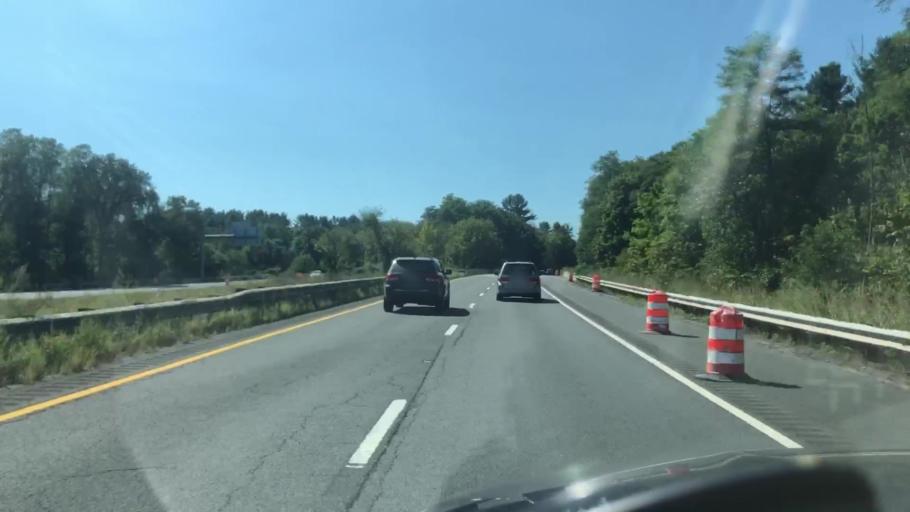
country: US
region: Massachusetts
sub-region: Franklin County
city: Bernardston
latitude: 42.6627
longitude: -72.5456
